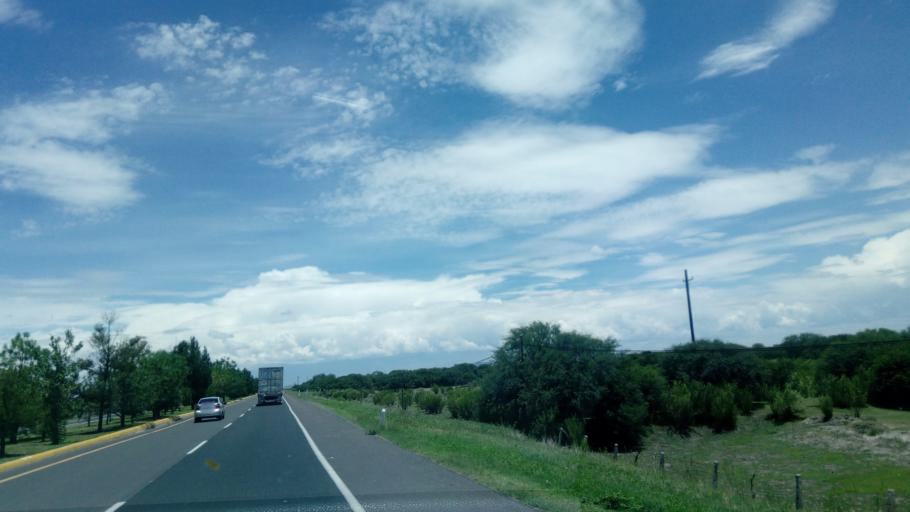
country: MX
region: Durango
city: Victoria de Durango
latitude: 24.1010
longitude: -104.5665
